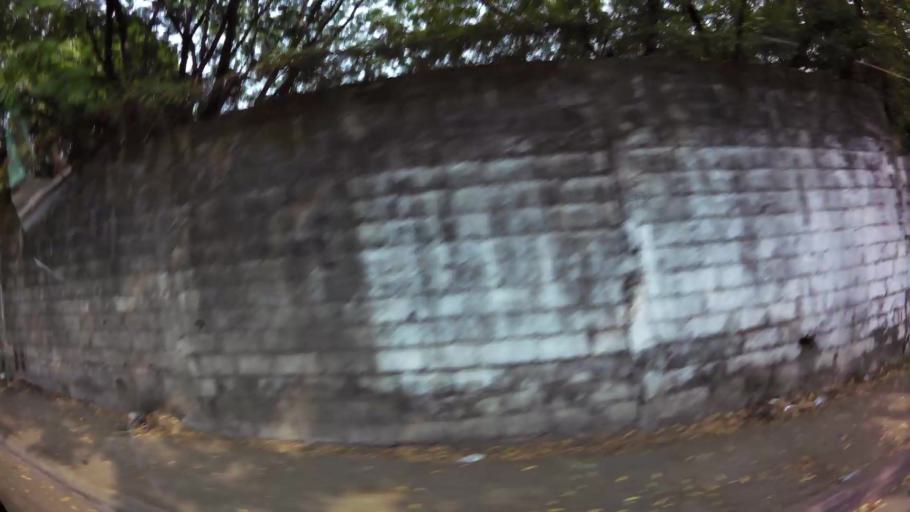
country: NI
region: Chinandega
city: Chinandega
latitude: 12.6342
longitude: -87.1212
